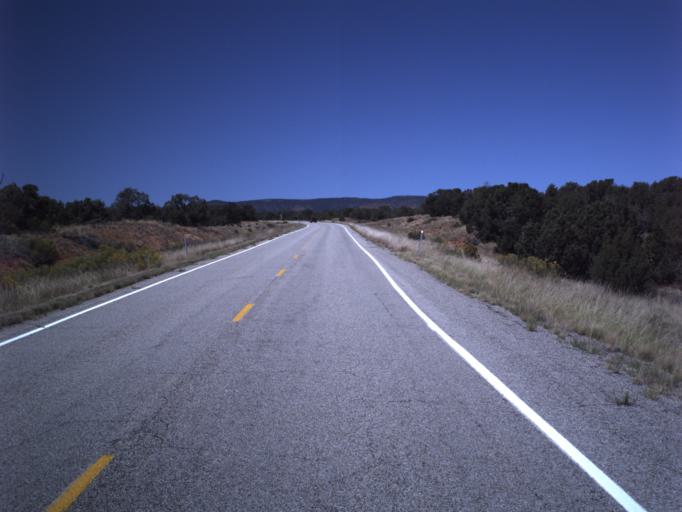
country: US
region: Utah
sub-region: San Juan County
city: Blanding
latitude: 37.5318
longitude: -109.6996
